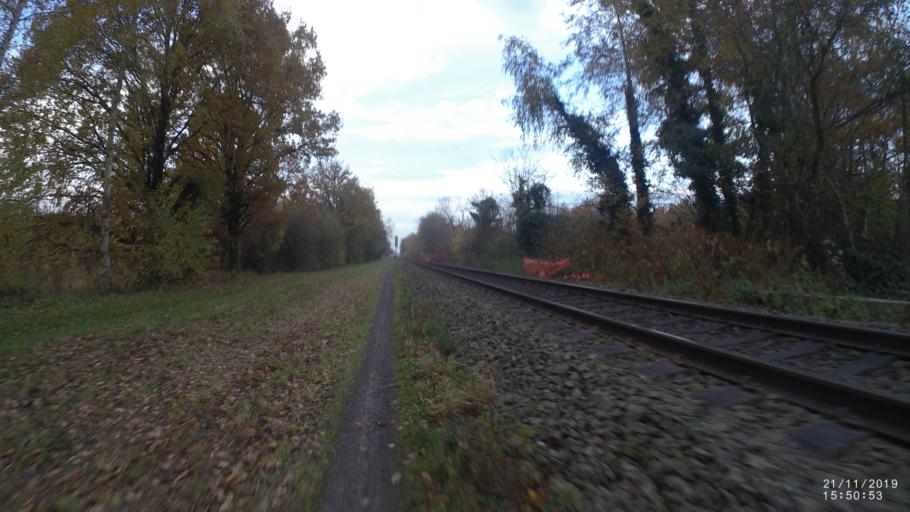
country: BE
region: Flanders
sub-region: Provincie Limburg
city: Zonhoven
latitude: 50.9842
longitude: 5.3491
